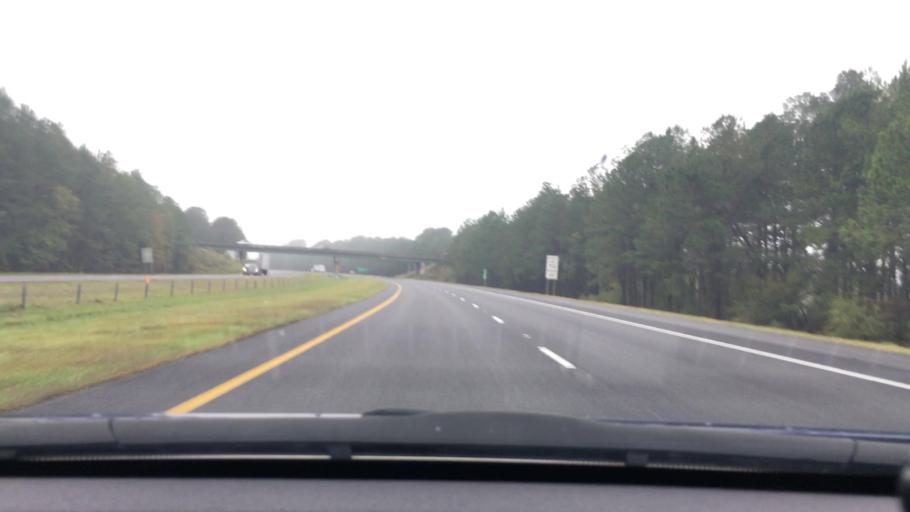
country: US
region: South Carolina
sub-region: Florence County
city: Timmonsville
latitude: 34.2083
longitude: -80.0386
